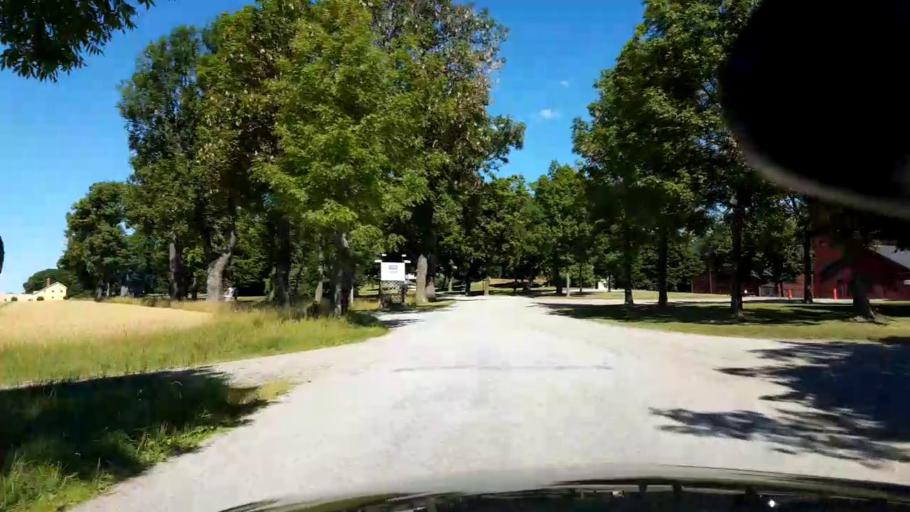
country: SE
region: Stockholm
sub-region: Sigtuna Kommun
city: Sigtuna
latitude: 59.6054
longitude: 17.6456
